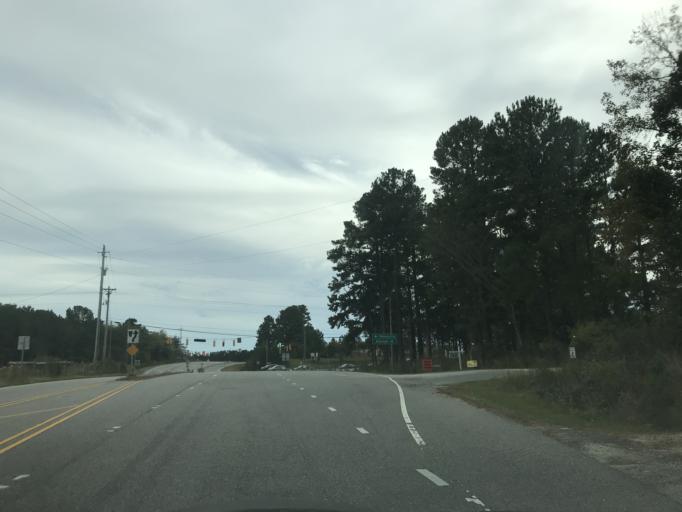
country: US
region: North Carolina
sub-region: Wake County
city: Rolesville
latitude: 35.8972
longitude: -78.5068
